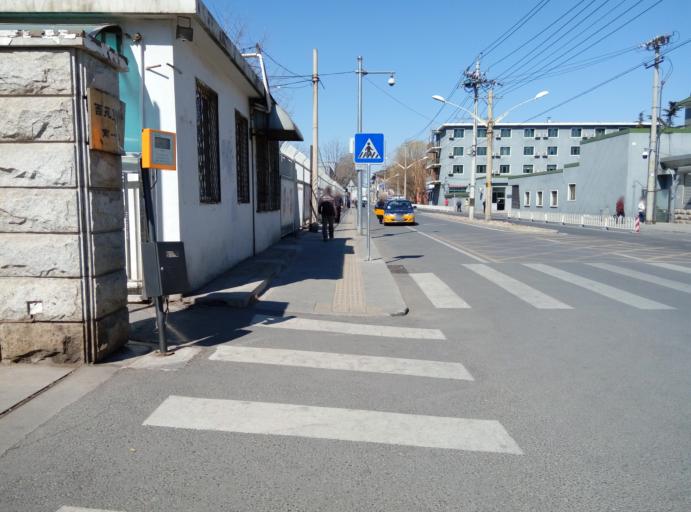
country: CN
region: Beijing
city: Haidian
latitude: 39.9901
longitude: 116.2865
